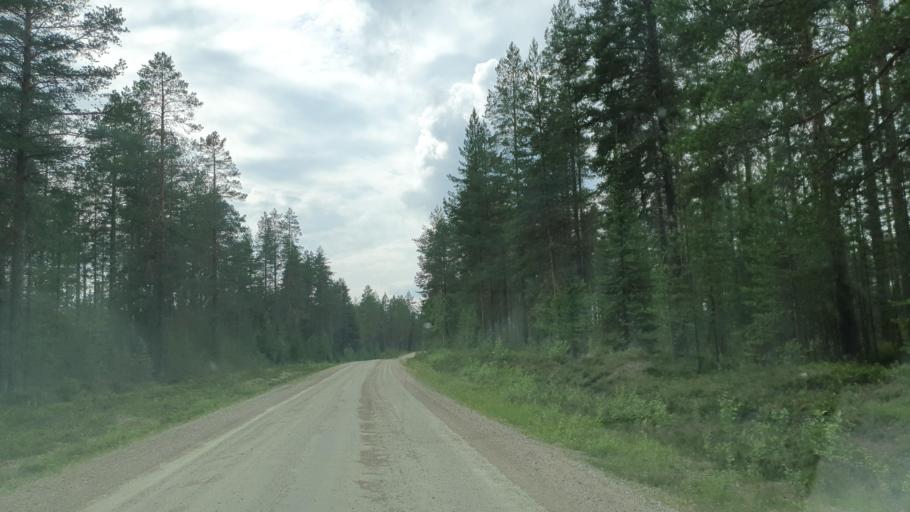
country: FI
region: Kainuu
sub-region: Kehys-Kainuu
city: Kuhmo
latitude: 64.7279
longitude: 29.7144
